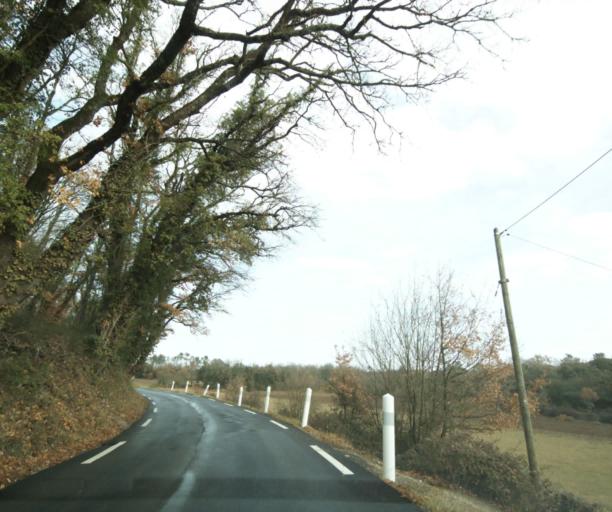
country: FR
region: Provence-Alpes-Cote d'Azur
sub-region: Departement du Var
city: Tourves
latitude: 43.4232
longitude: 5.9339
